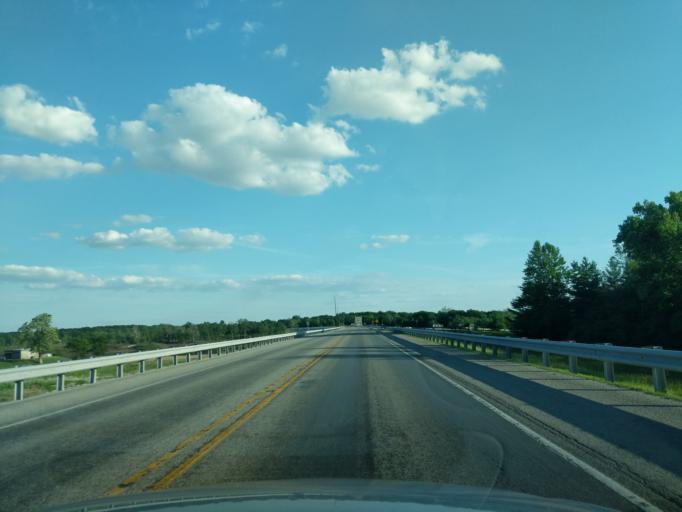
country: US
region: Indiana
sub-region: Huntington County
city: Huntington
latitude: 40.8508
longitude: -85.4684
